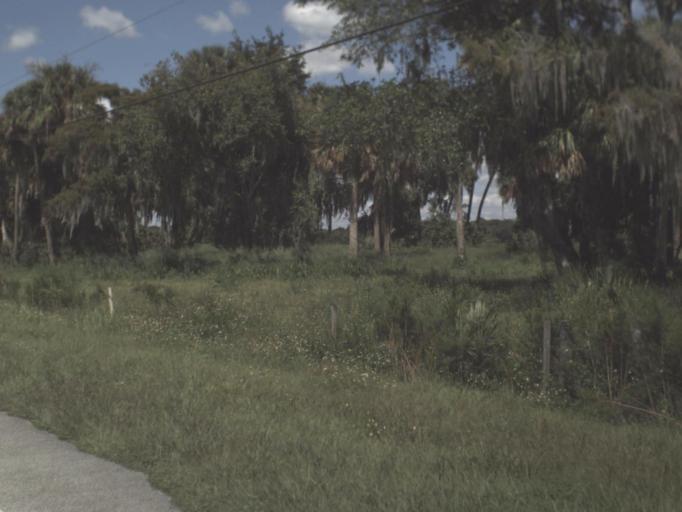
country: US
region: Florida
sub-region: Okeechobee County
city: Taylor Creek
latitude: 27.1772
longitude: -80.7301
